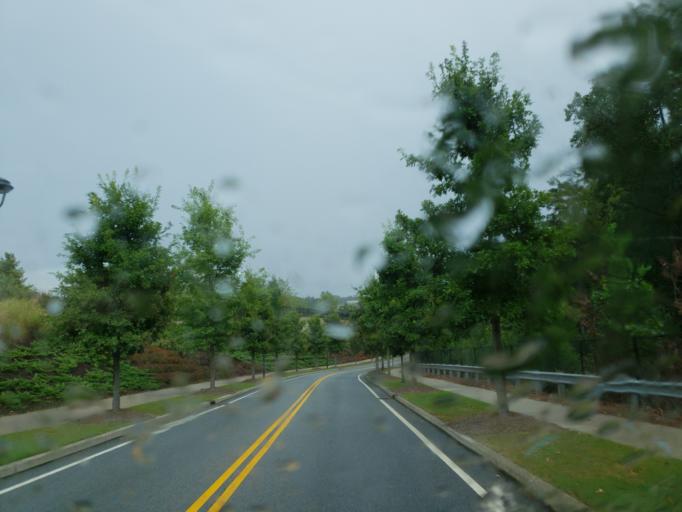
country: US
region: Georgia
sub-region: Cherokee County
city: Woodstock
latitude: 34.1183
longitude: -84.5276
